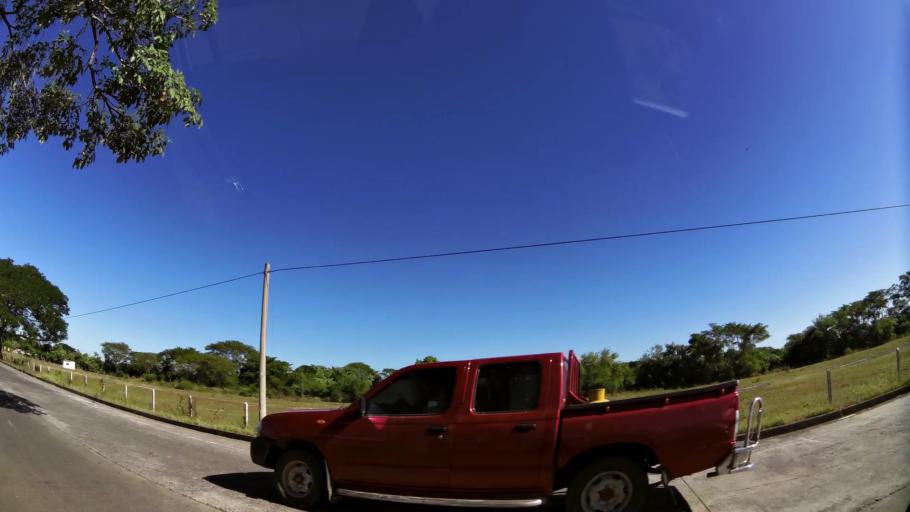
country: SV
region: San Miguel
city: San Miguel
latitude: 13.4449
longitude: -88.1292
